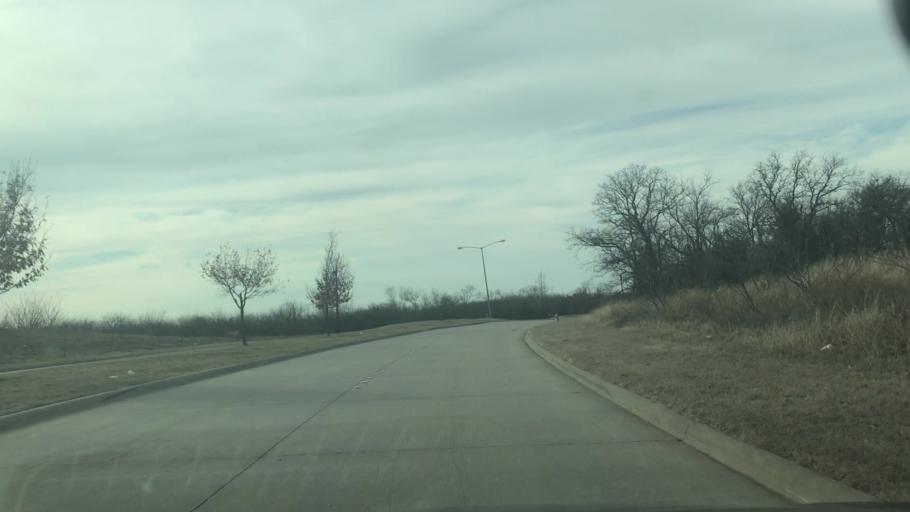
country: US
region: Texas
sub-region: Dallas County
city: Coppell
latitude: 32.9976
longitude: -97.0210
